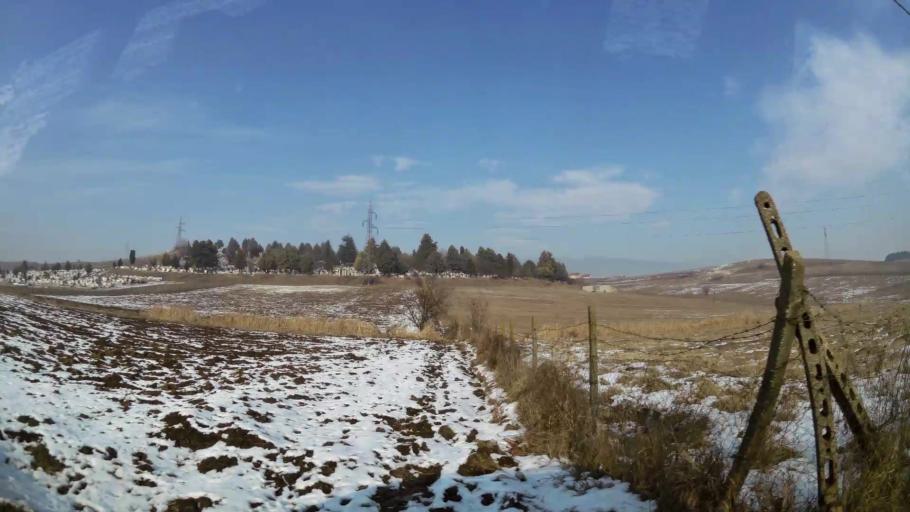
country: MK
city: Creshevo
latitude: 42.0140
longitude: 21.4931
